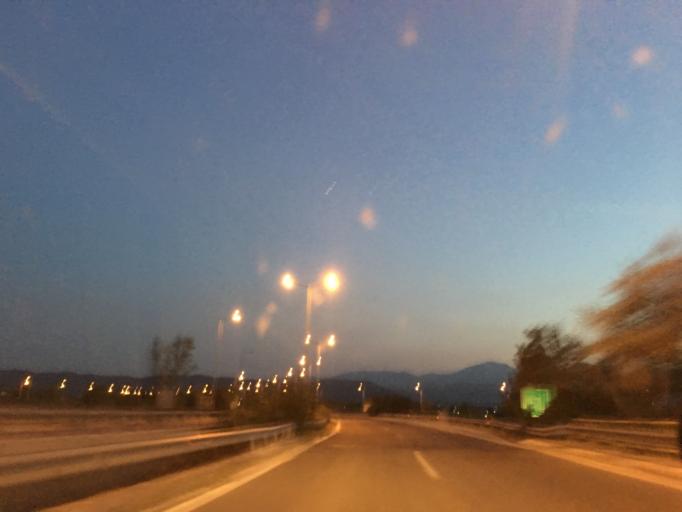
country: MK
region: Petrovec
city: Petrovec
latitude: 41.9387
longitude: 21.6267
